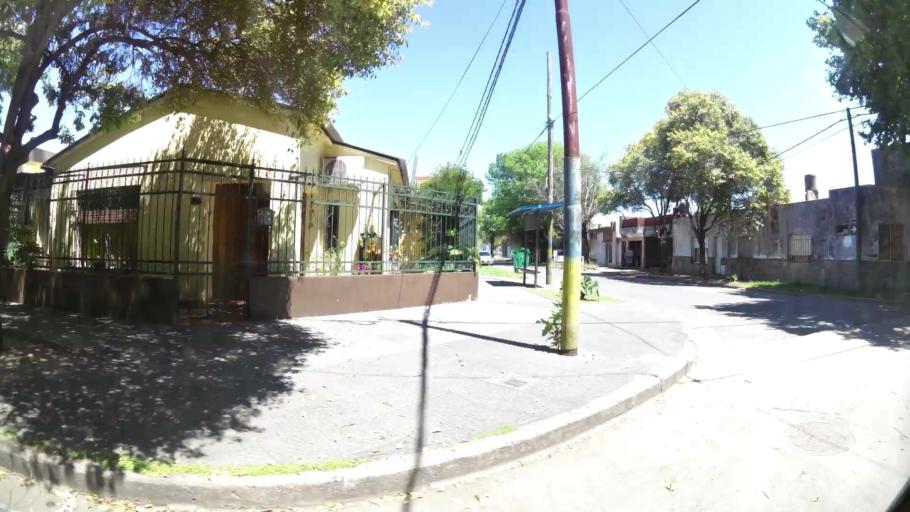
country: AR
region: Santa Fe
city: Perez
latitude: -32.9437
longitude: -60.7172
